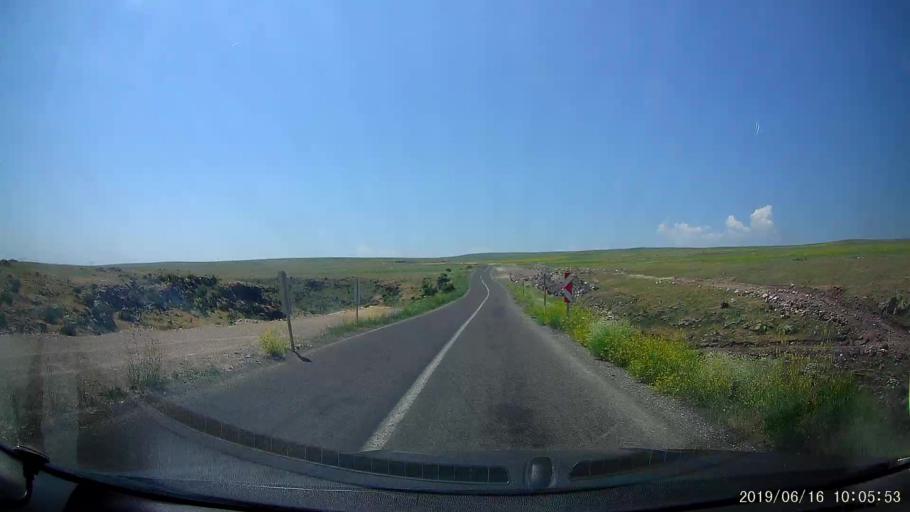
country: TR
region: Kars
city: Digor
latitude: 40.2641
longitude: 43.5399
